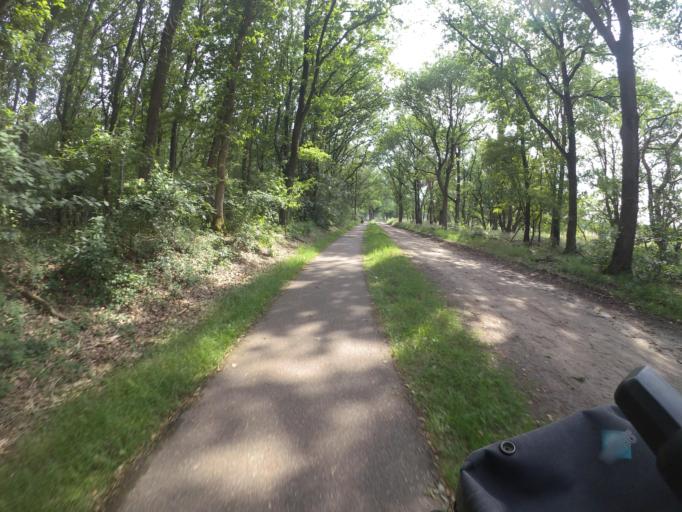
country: NL
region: Overijssel
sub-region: Gemeente Twenterand
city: Den Ham
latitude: 52.4688
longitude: 6.3919
